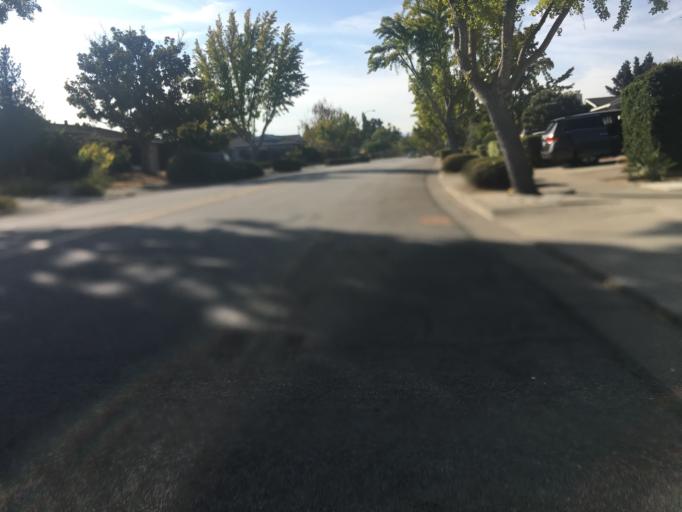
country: US
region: California
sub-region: Santa Clara County
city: Sunnyvale
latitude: 37.3462
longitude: -122.0616
